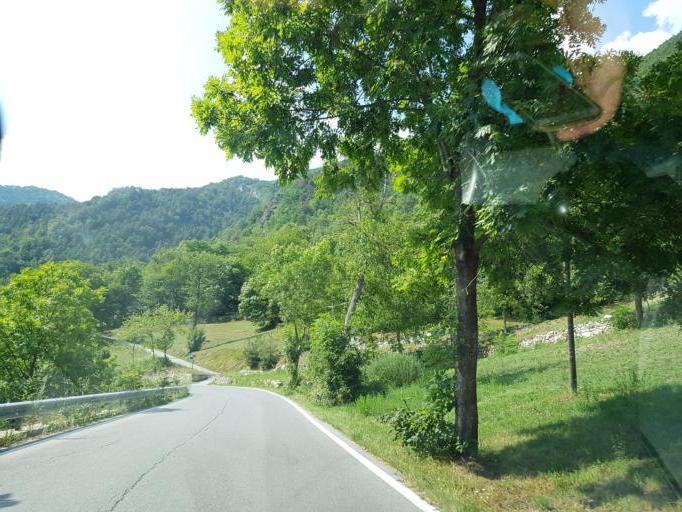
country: IT
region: Piedmont
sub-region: Provincia di Cuneo
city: San Damiano Macra
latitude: 44.4933
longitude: 7.2410
